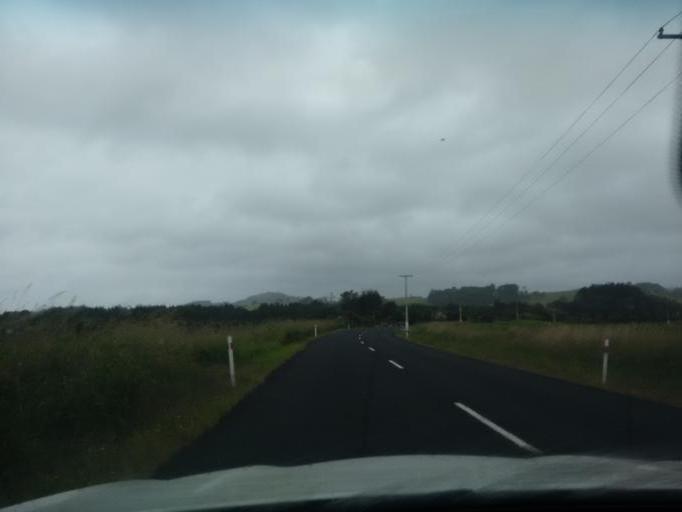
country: NZ
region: Waikato
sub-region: Thames-Coromandel District
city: Whitianga
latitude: -36.8684
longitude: 175.8060
